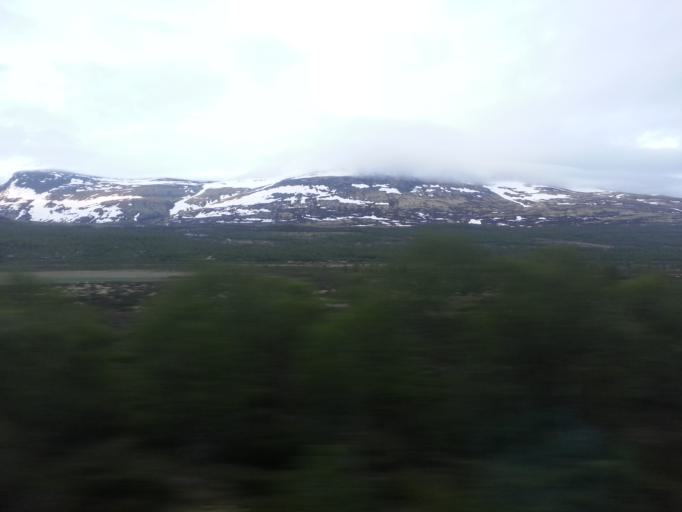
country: NO
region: Oppland
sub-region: Dovre
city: Dovre
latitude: 62.1622
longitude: 9.3465
